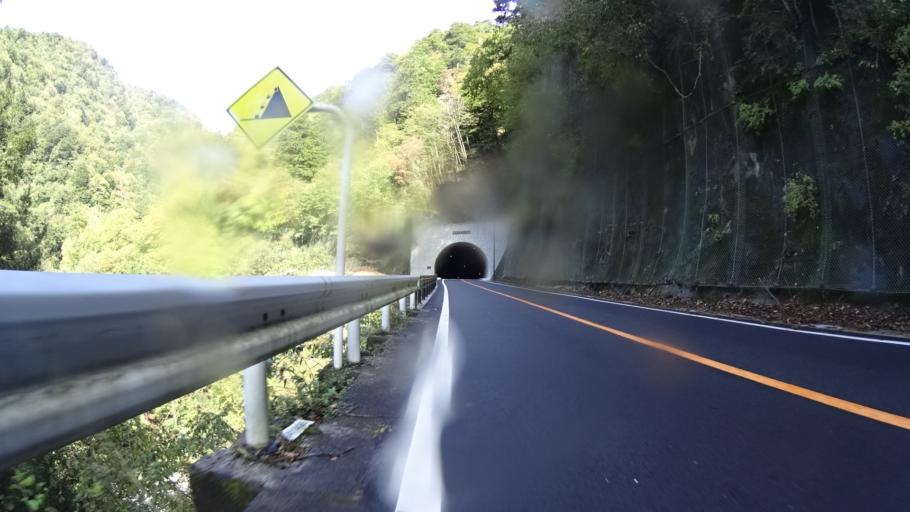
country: JP
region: Yamanashi
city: Enzan
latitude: 35.7991
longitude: 138.8654
